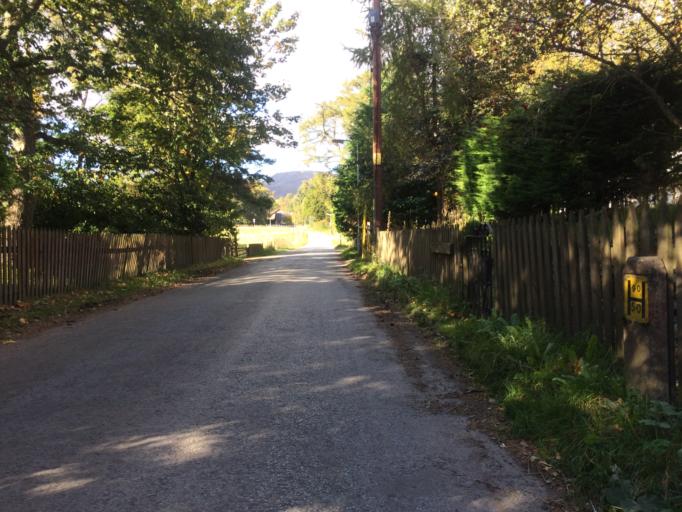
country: GB
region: Scotland
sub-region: Highland
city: Kingussie
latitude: 57.0607
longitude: -4.1232
